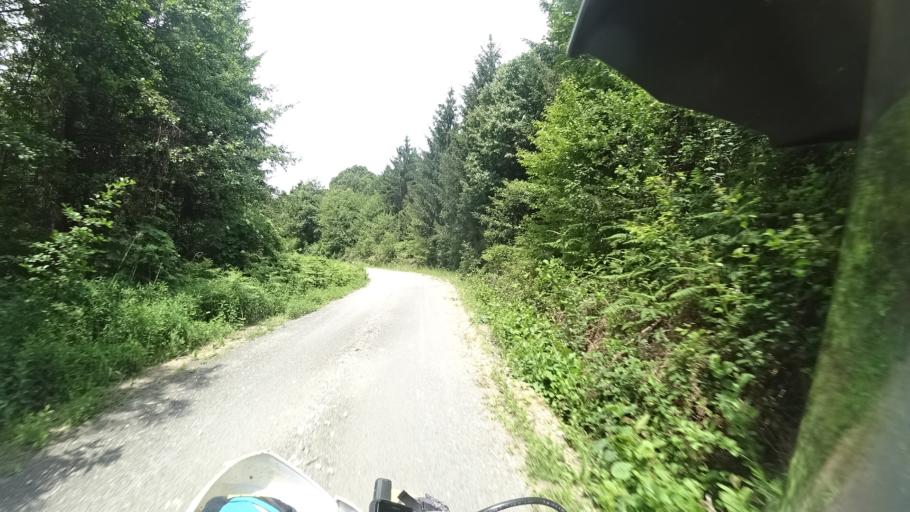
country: HR
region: Karlovacka
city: Vojnic
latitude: 45.2714
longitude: 15.7393
